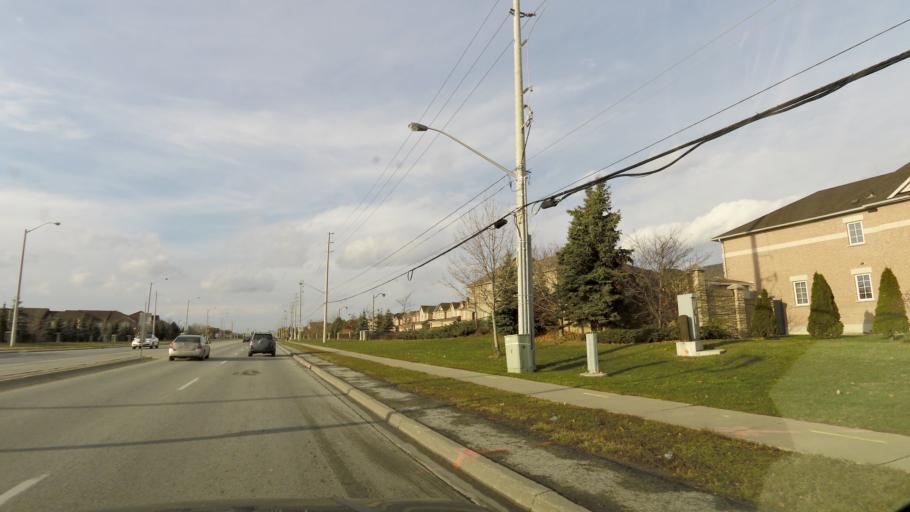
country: CA
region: Ontario
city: Brampton
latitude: 43.7780
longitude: -79.6709
